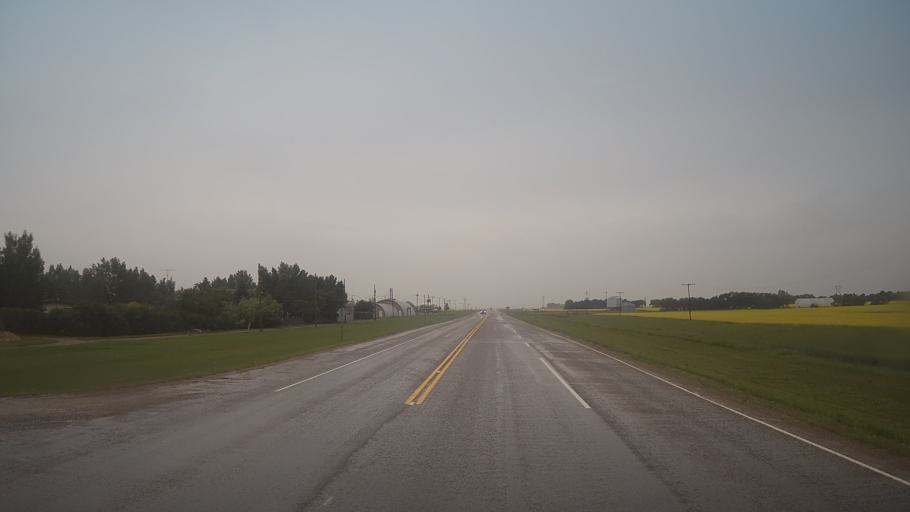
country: CA
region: Saskatchewan
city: Wilkie
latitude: 52.2020
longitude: -108.4490
